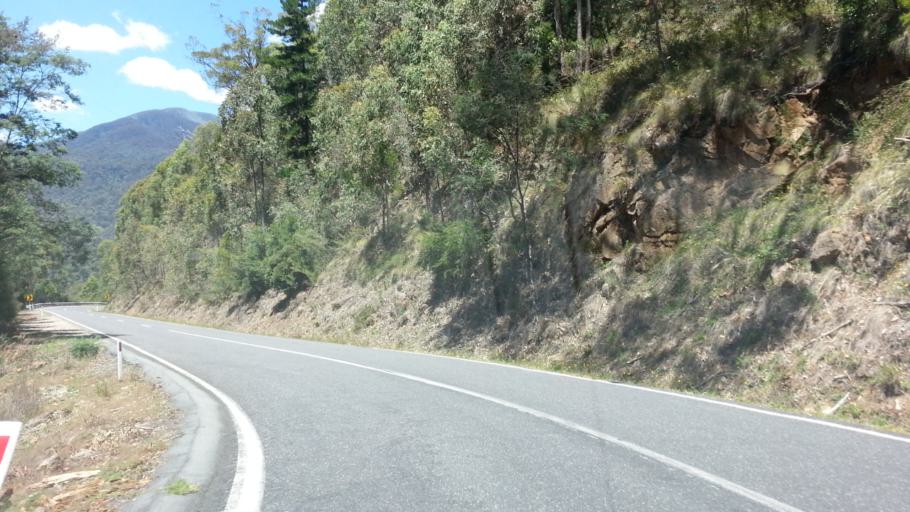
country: AU
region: Victoria
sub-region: Alpine
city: Mount Beauty
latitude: -36.7617
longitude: 147.2064
